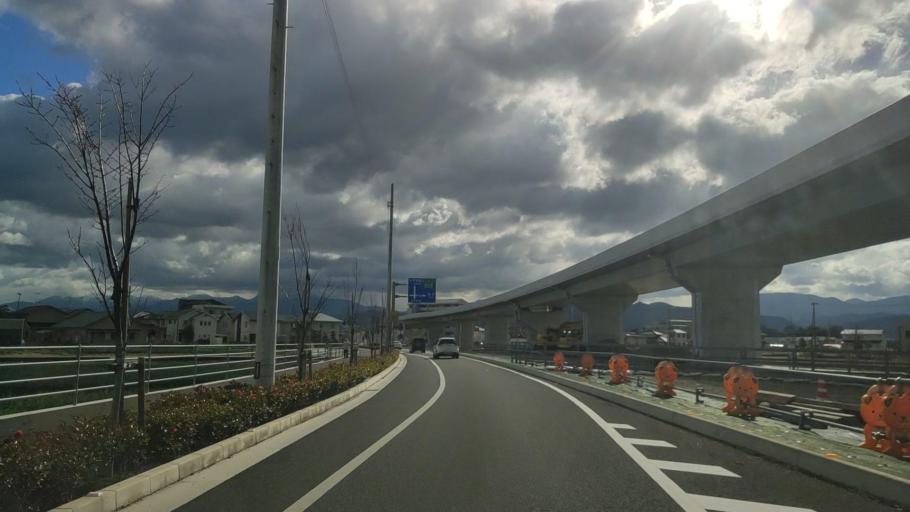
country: JP
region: Ehime
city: Masaki-cho
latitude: 33.8131
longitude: 132.7220
